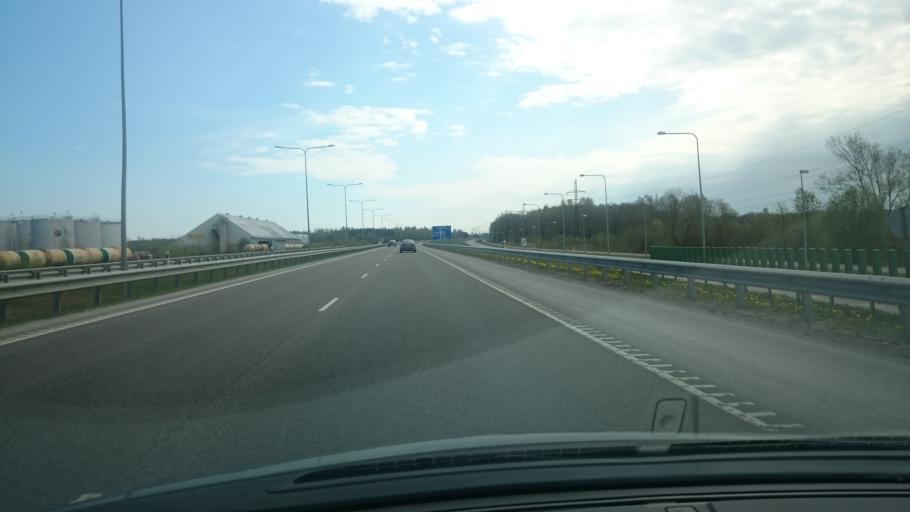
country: EE
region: Harju
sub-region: Maardu linn
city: Maardu
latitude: 59.4519
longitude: 25.0004
